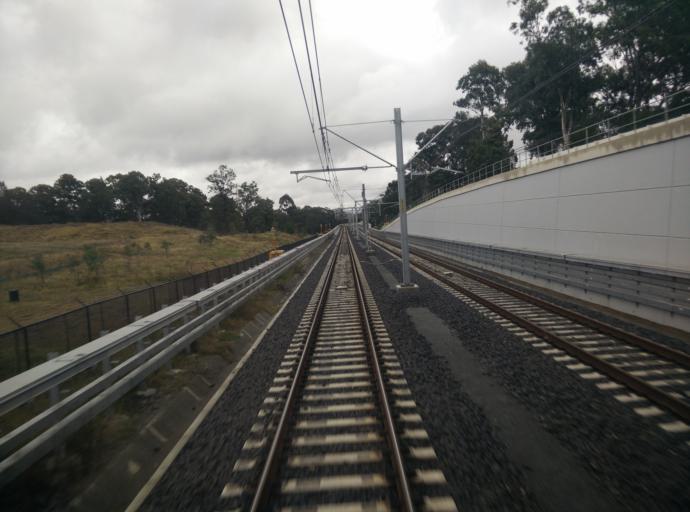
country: AU
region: New South Wales
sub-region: Blacktown
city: Rouse Hill
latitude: -33.6893
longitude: 150.9177
